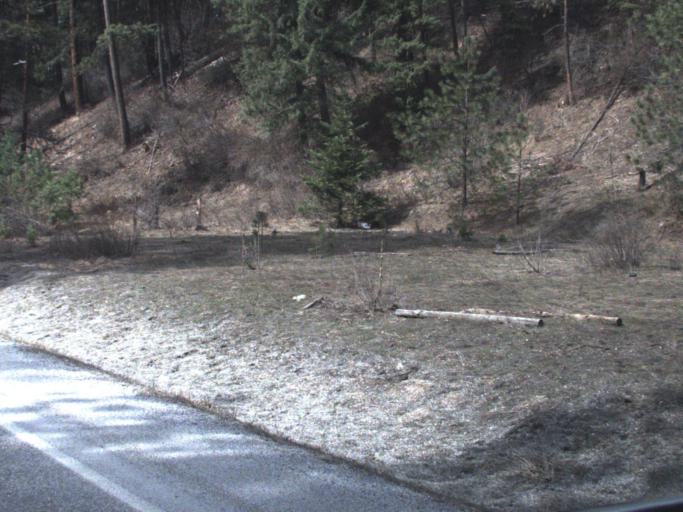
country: US
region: Washington
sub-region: Pend Oreille County
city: Newport
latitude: 48.4711
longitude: -117.3114
